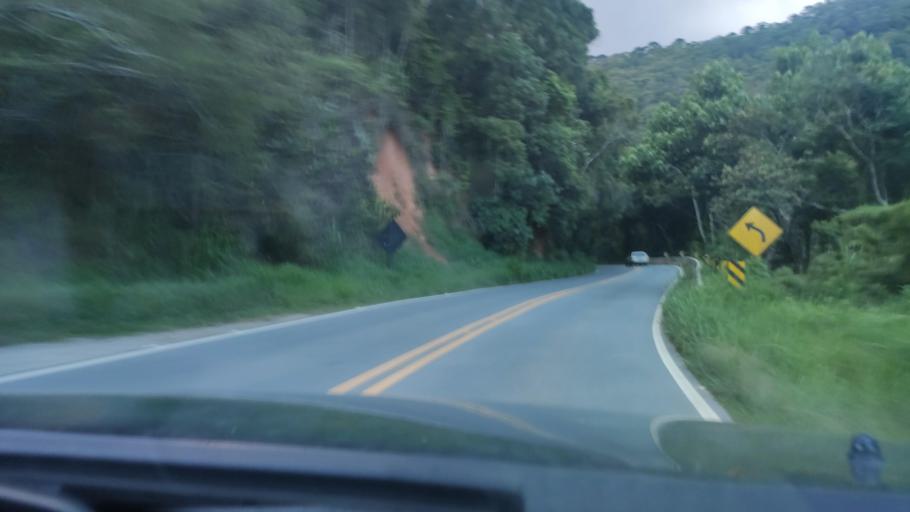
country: BR
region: Sao Paulo
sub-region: Campos Do Jordao
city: Campos do Jordao
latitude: -22.8301
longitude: -45.6947
